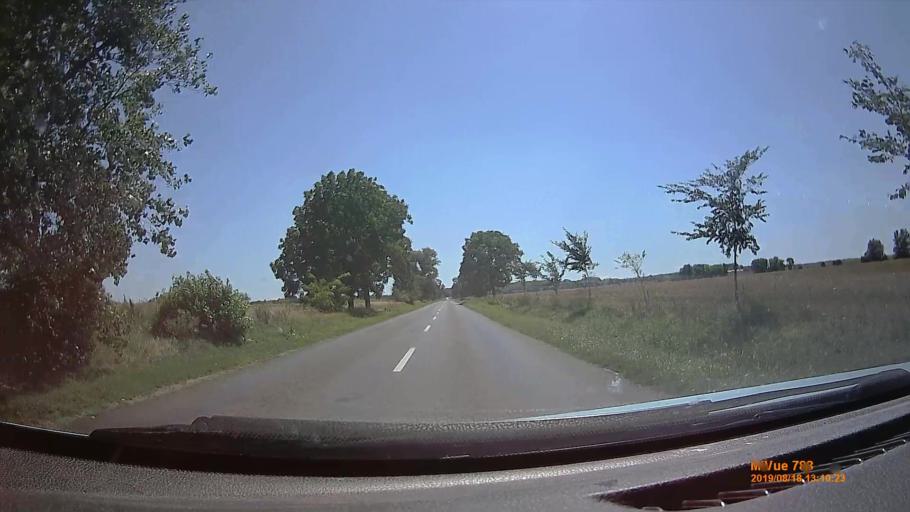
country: HU
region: Fejer
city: Kaloz
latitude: 46.9155
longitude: 18.5163
